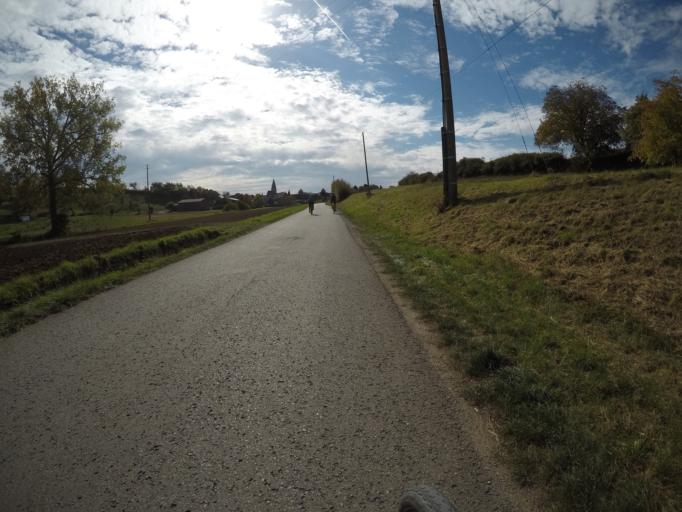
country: DE
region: Baden-Wuerttemberg
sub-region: Regierungsbezirk Stuttgart
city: Hildrizhausen
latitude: 48.6305
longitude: 8.9677
